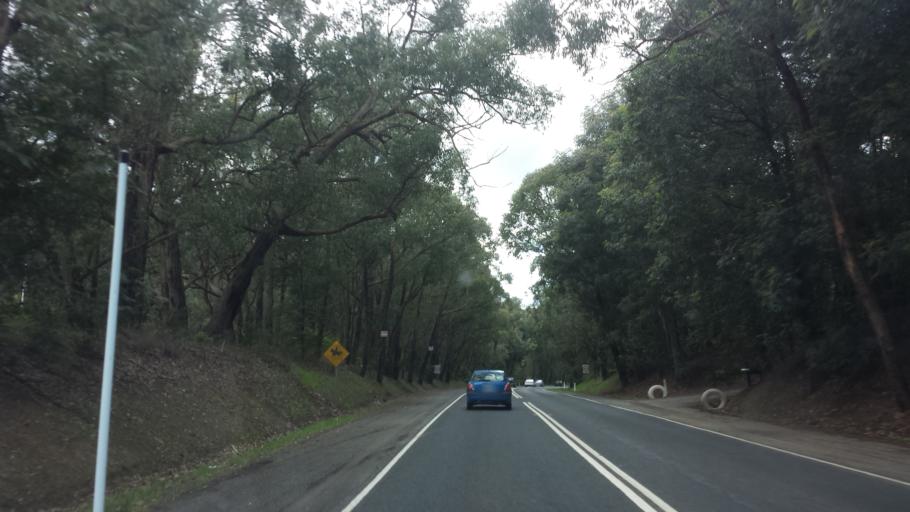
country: AU
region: Victoria
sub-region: Yarra Ranges
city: Selby
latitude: -37.9369
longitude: 145.4046
